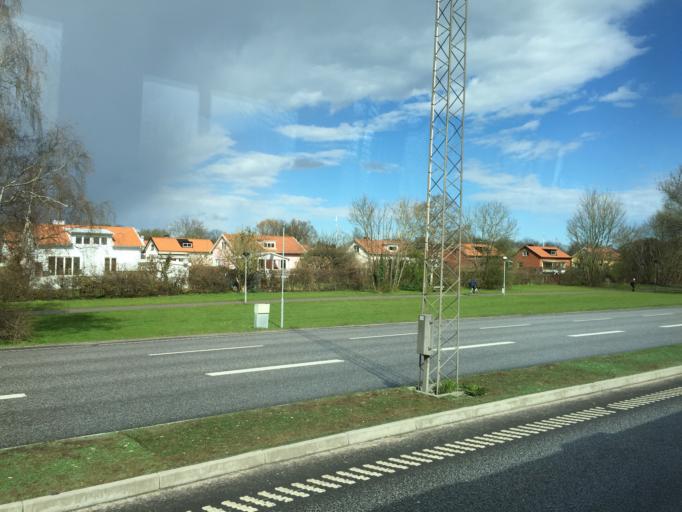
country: SE
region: Skane
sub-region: Lunds Kommun
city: Lund
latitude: 55.6976
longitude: 13.2207
